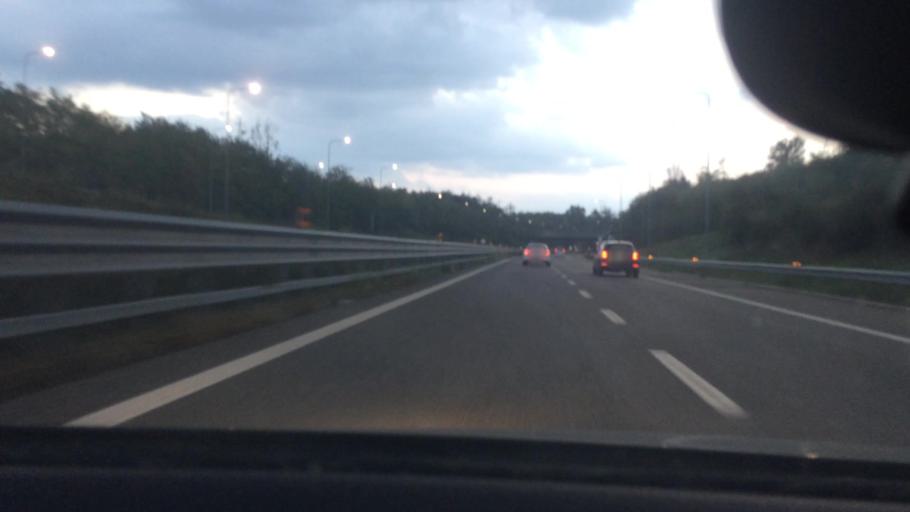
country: IT
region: Lombardy
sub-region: Citta metropolitana di Milano
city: Castano Primo
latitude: 45.5625
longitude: 8.7844
